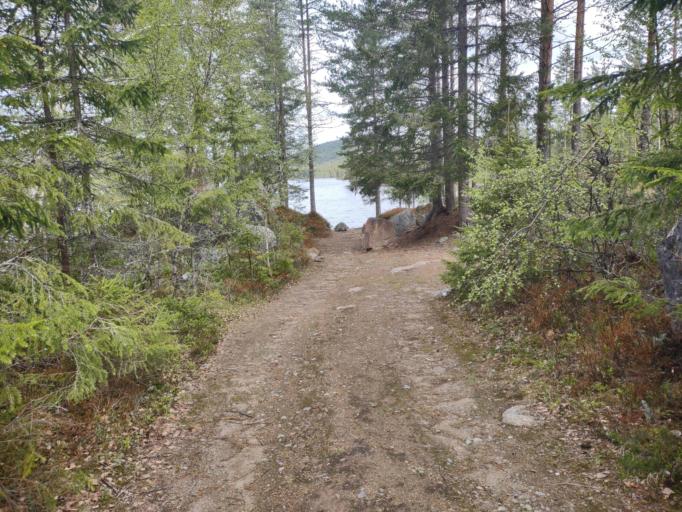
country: NO
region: Oppland
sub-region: Lunner
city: Grua
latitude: 60.2838
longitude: 10.7772
